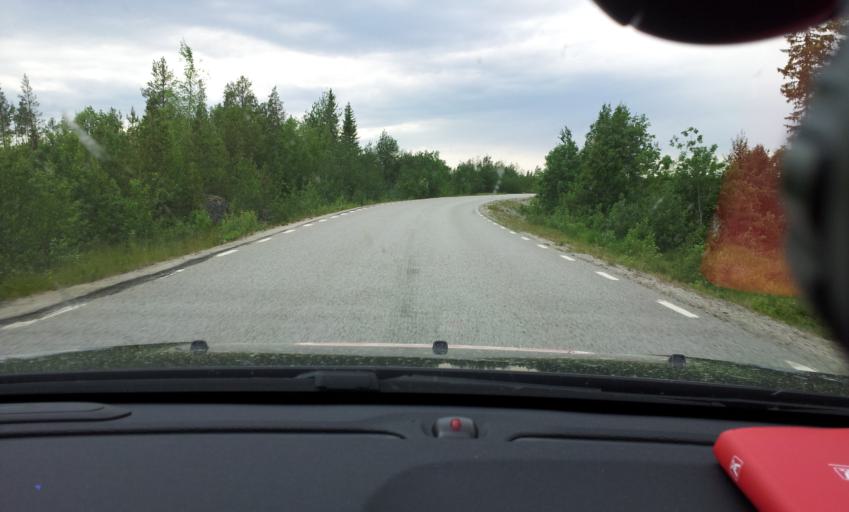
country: SE
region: Jaemtland
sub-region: Bergs Kommun
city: Hoverberg
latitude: 62.6770
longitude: 14.7030
